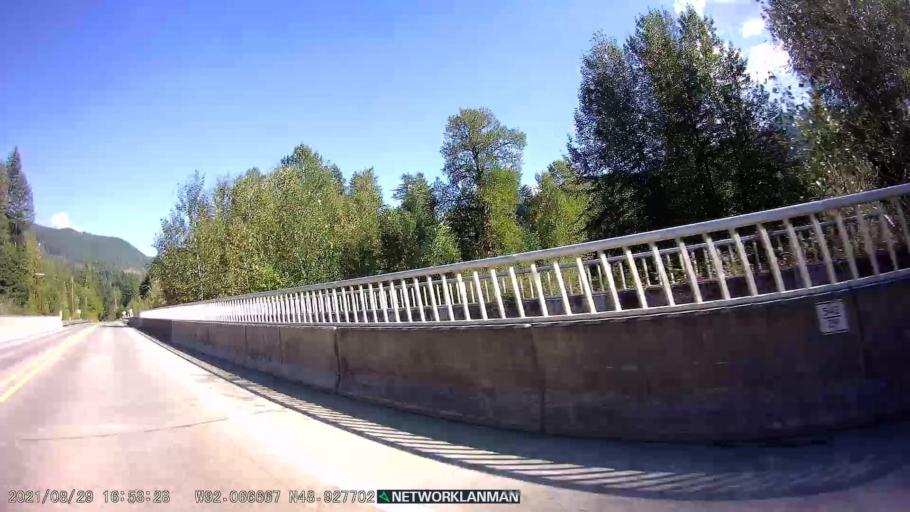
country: US
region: Washington
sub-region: Whatcom County
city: Peaceful Valley
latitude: 48.9291
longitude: -122.0302
